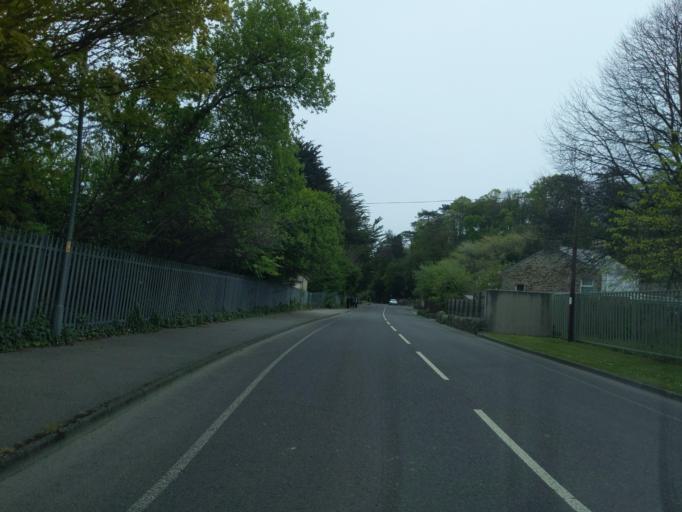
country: GB
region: England
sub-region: Cornwall
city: Par
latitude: 50.3554
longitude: -4.7116
